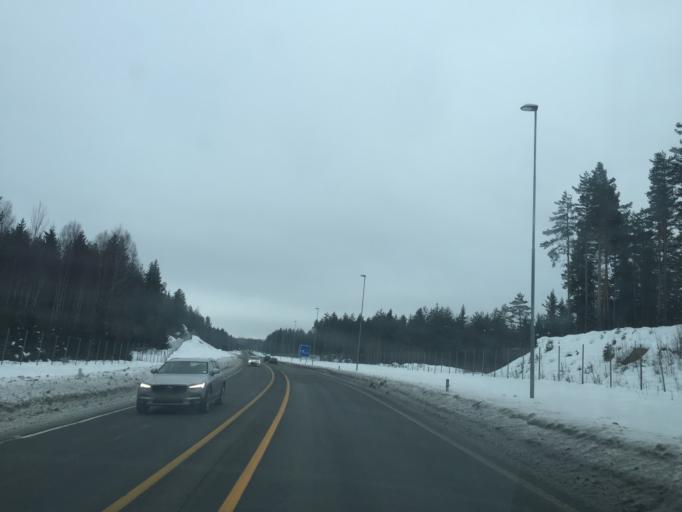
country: NO
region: Hedmark
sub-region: Stange
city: Stange
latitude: 60.7060
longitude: 11.2775
